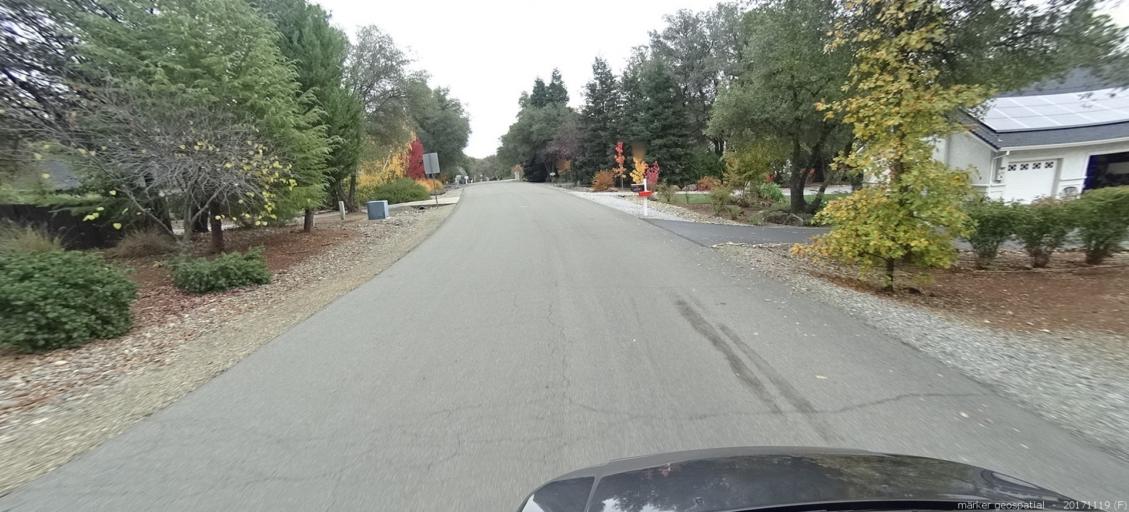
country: US
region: California
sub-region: Shasta County
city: Redding
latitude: 40.4949
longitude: -122.4108
